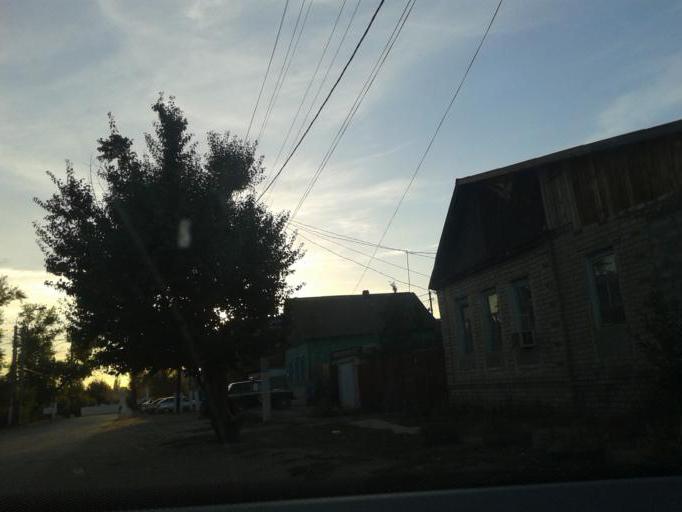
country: RU
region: Volgograd
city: Krasnoslobodsk
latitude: 48.7072
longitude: 44.5644
